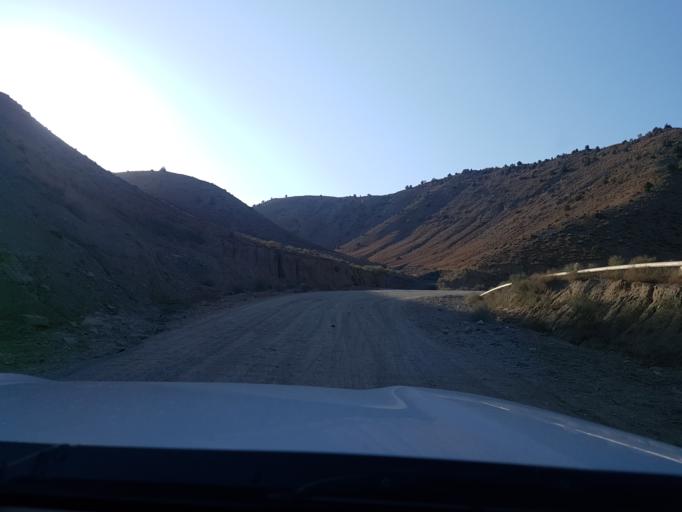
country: TM
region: Ahal
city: Baharly
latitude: 38.4463
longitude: 57.0489
